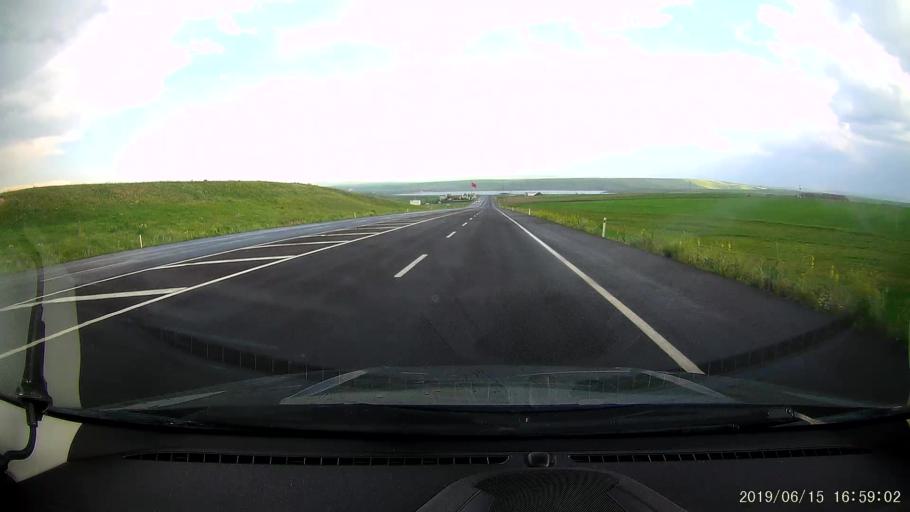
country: TR
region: Kars
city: Susuz
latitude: 40.7570
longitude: 43.1478
